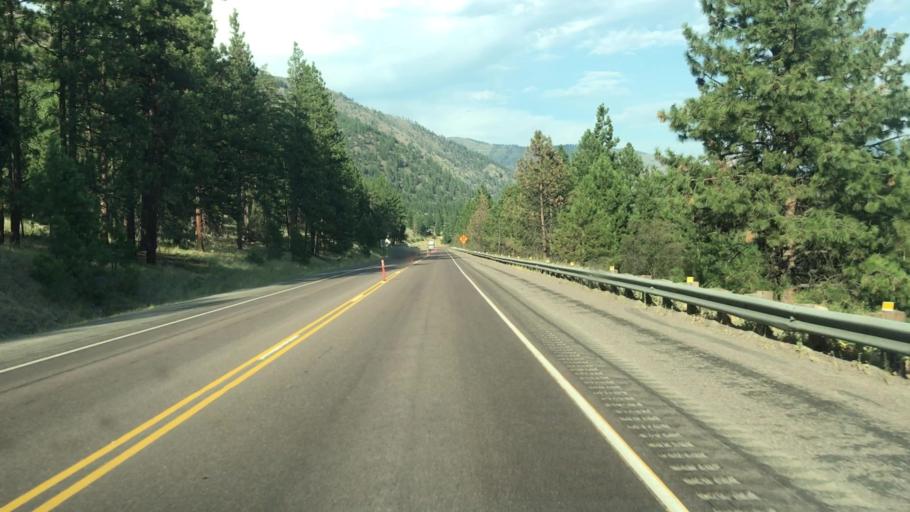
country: US
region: Montana
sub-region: Mineral County
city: Superior
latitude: 47.0171
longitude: -114.6862
